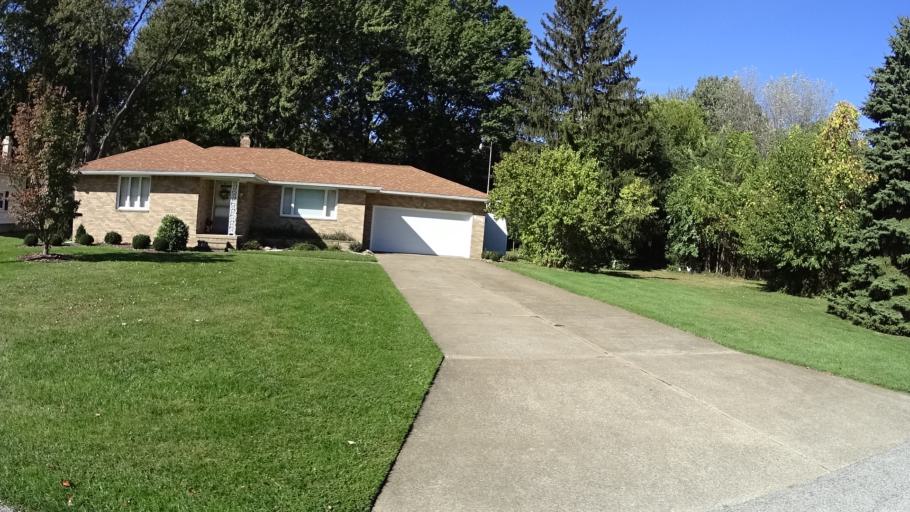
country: US
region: Ohio
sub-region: Lorain County
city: Lorain
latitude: 41.4199
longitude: -82.1765
